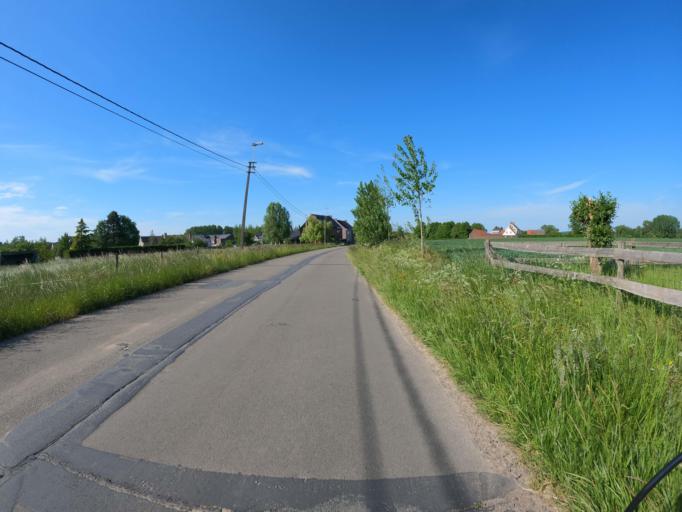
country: BE
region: Flanders
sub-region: Provincie Oost-Vlaanderen
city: Oosterzele
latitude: 50.9311
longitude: 3.7531
